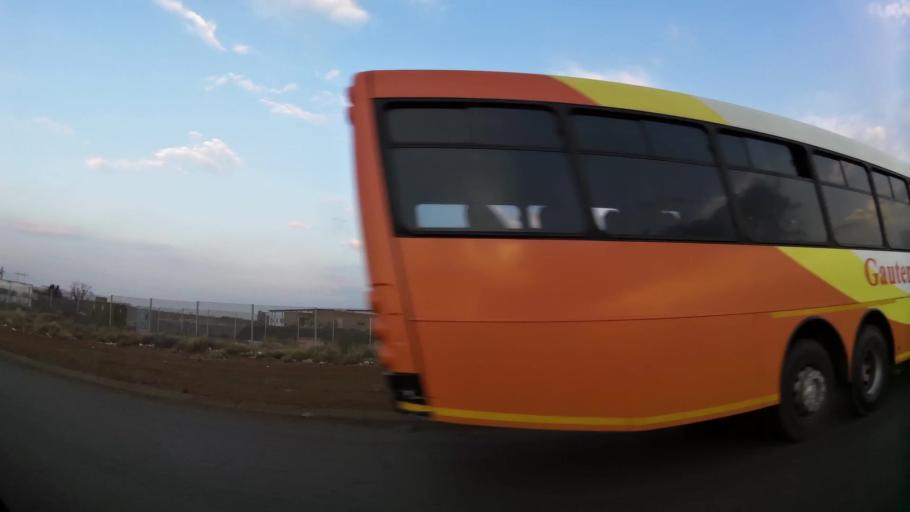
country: ZA
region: Gauteng
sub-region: City of Johannesburg Metropolitan Municipality
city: Orange Farm
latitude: -26.5608
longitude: 27.8602
